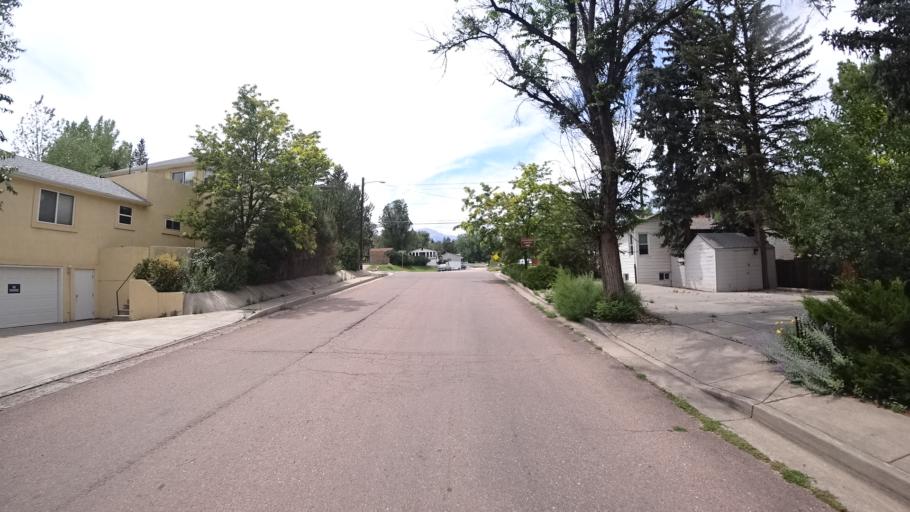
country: US
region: Colorado
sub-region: El Paso County
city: Colorado Springs
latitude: 38.8555
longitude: -104.8353
